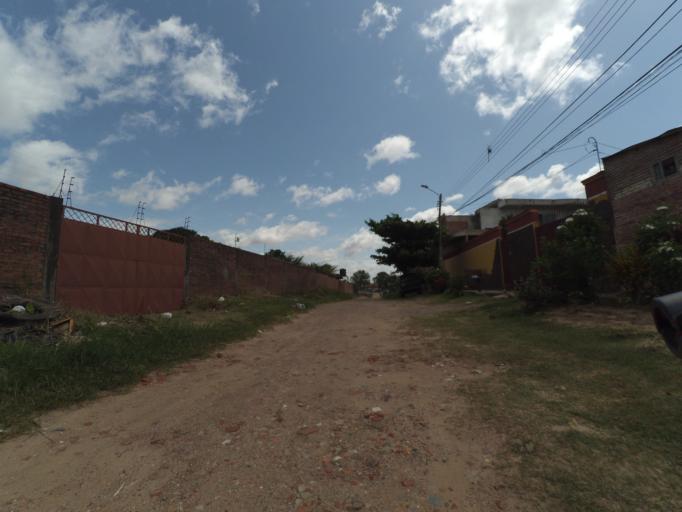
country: BO
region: Santa Cruz
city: Santa Cruz de la Sierra
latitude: -17.8055
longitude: -63.2261
